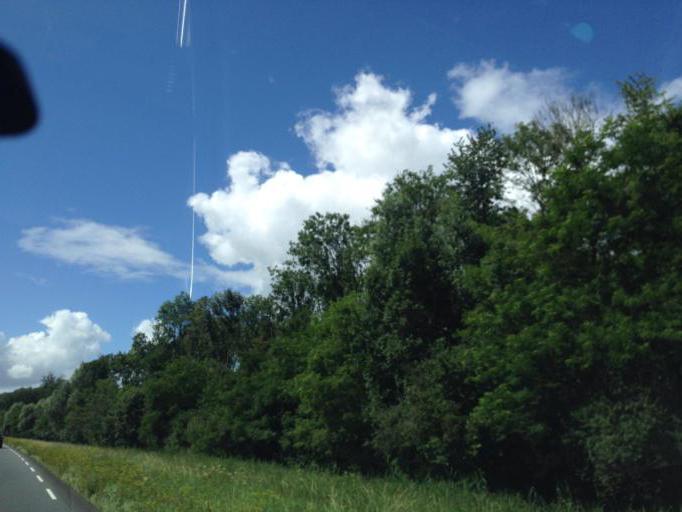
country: NL
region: Overijssel
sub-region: Gemeente Kampen
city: Kampen
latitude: 52.5458
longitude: 5.8222
